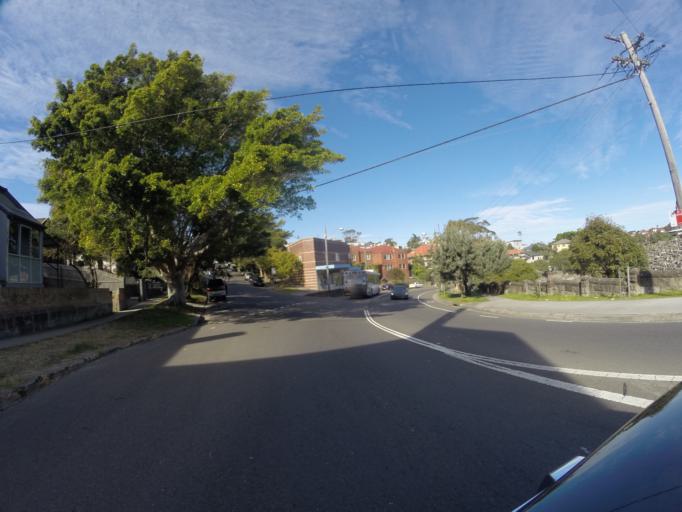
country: AU
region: New South Wales
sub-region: Randwick
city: South Coogee
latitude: -33.9287
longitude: 151.2553
